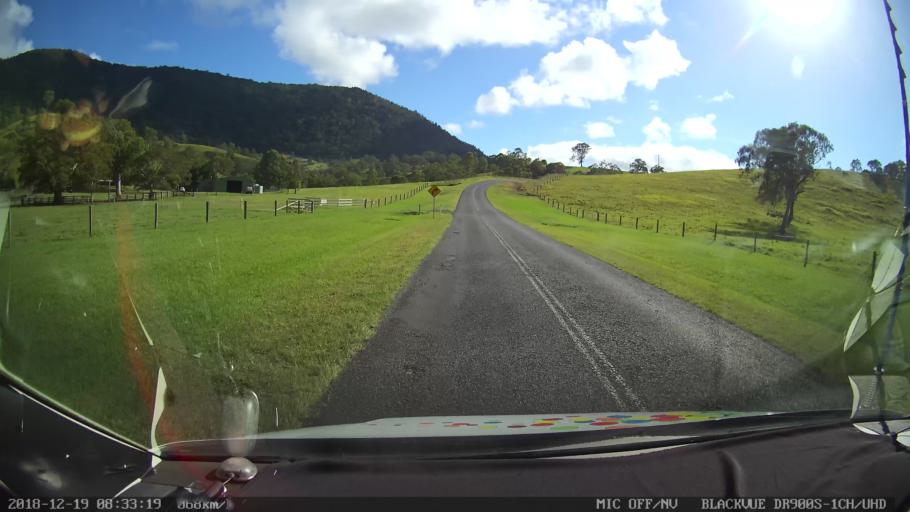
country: AU
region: New South Wales
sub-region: Kyogle
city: Kyogle
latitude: -28.3210
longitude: 152.9490
